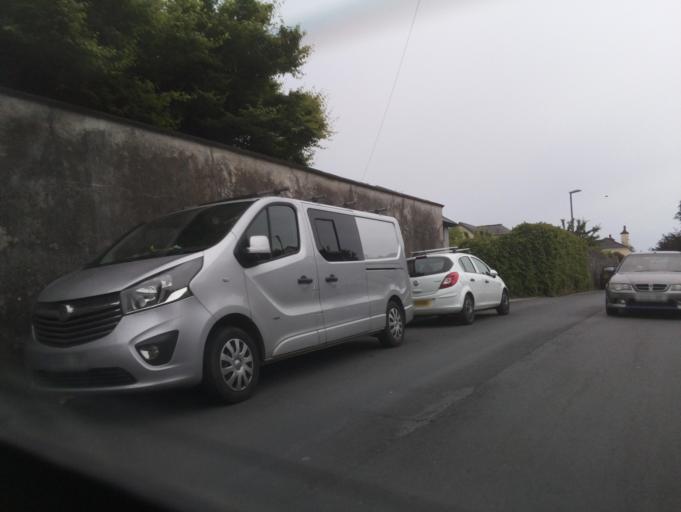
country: GB
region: England
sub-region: Devon
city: Ashburton
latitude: 50.5188
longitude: -3.7487
